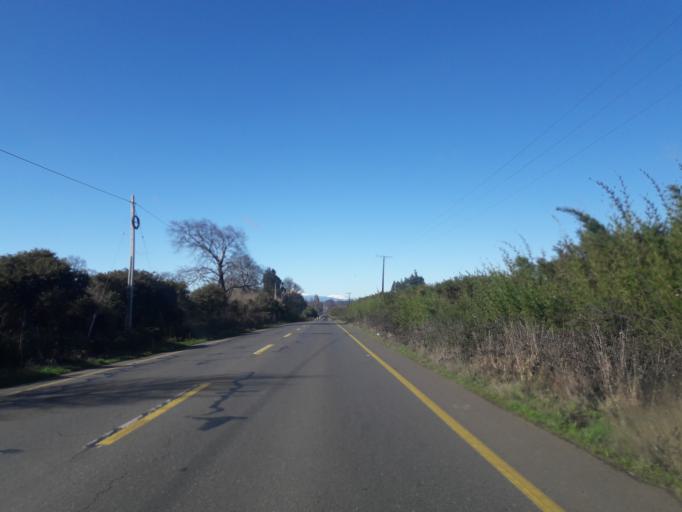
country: CL
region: Araucania
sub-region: Provincia de Malleco
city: Victoria
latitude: -38.2564
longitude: -72.2692
